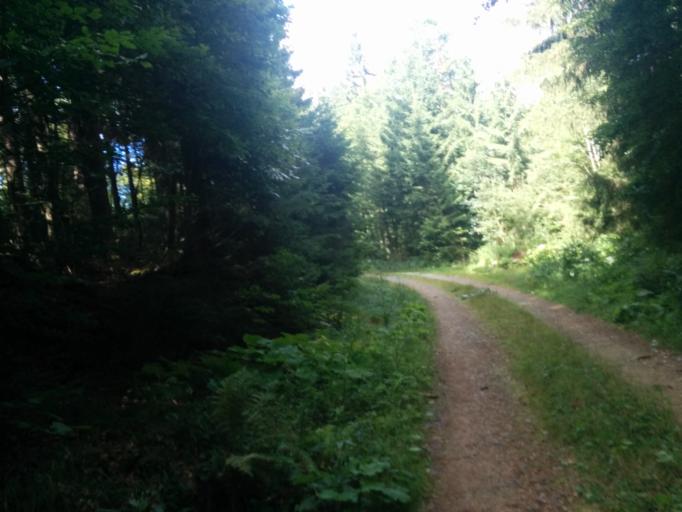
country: AT
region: Upper Austria
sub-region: Politischer Bezirk Rohrbach
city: Ulrichsberg
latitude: 48.7079
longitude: 13.9616
